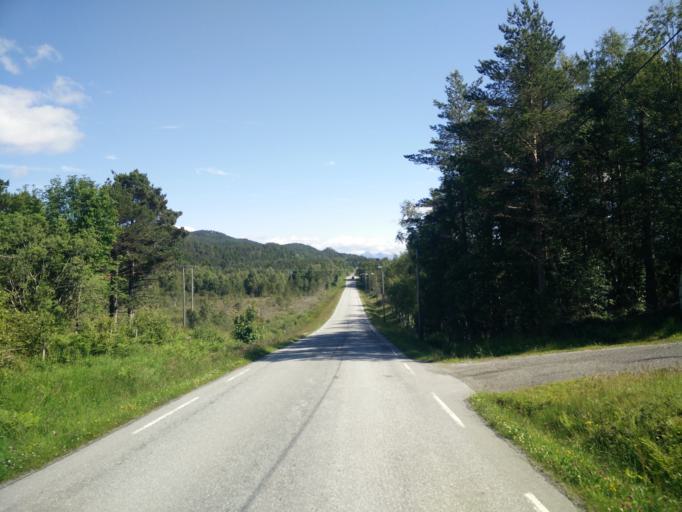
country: NO
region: More og Romsdal
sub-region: Kristiansund
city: Rensvik
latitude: 63.0288
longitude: 7.8056
